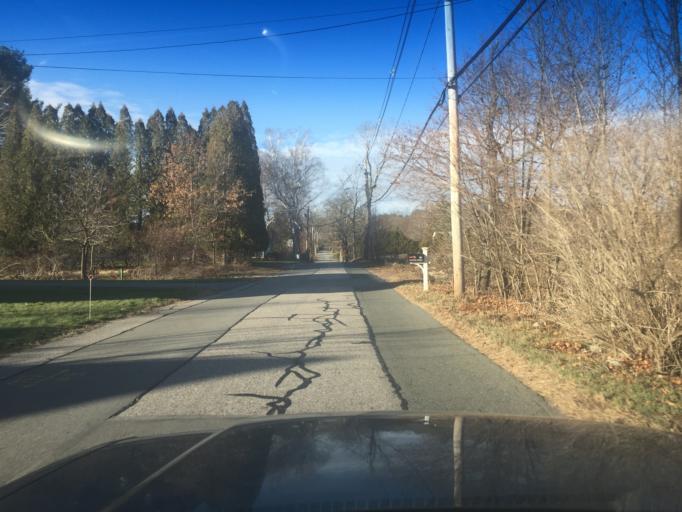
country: US
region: Massachusetts
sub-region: Middlesex County
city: Hopkinton
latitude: 42.2340
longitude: -71.4892
